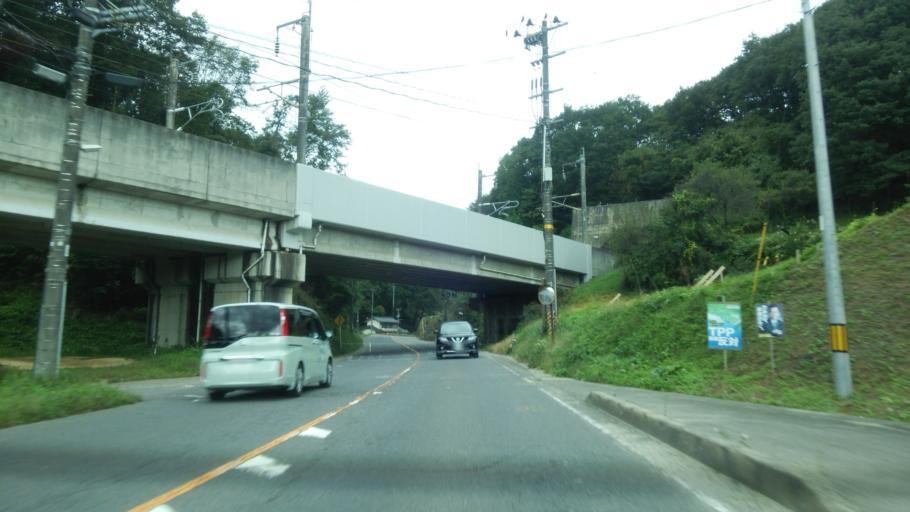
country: JP
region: Fukushima
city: Sukagawa
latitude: 37.1542
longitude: 140.2183
